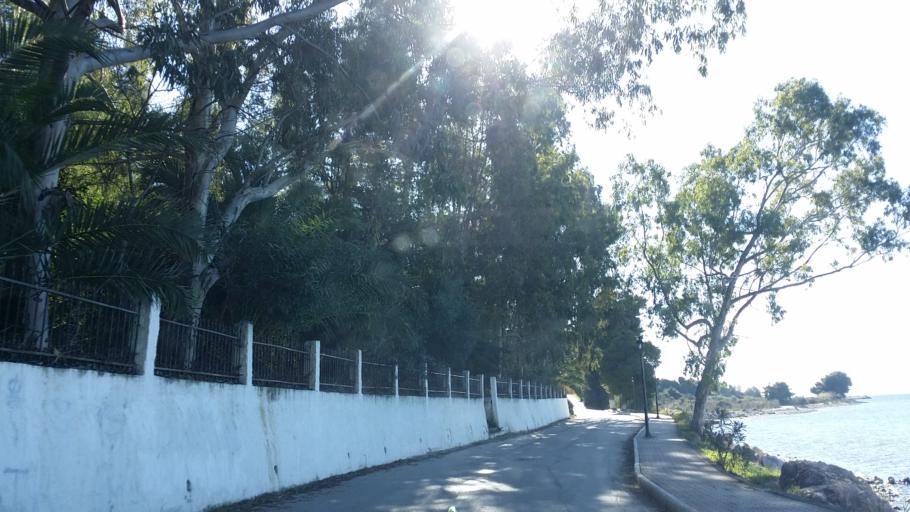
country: GR
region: West Greece
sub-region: Nomos Aitolias kai Akarnanias
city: Palairos
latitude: 38.7767
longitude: 20.8814
